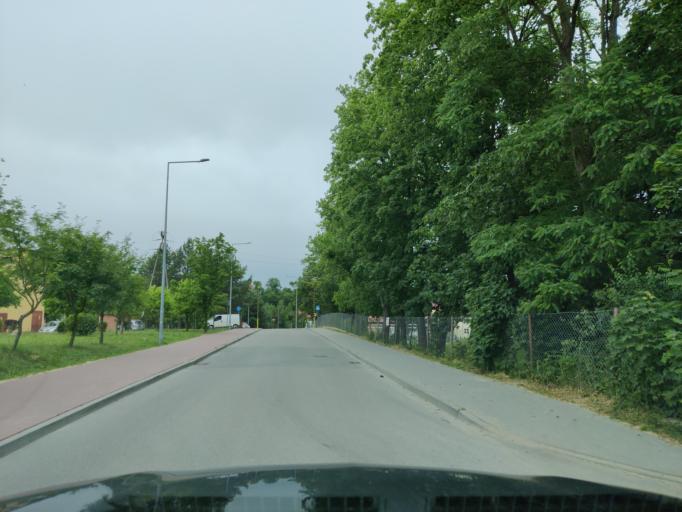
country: PL
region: Warmian-Masurian Voivodeship
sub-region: Powiat gizycki
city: Ryn
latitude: 53.9352
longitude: 21.5385
